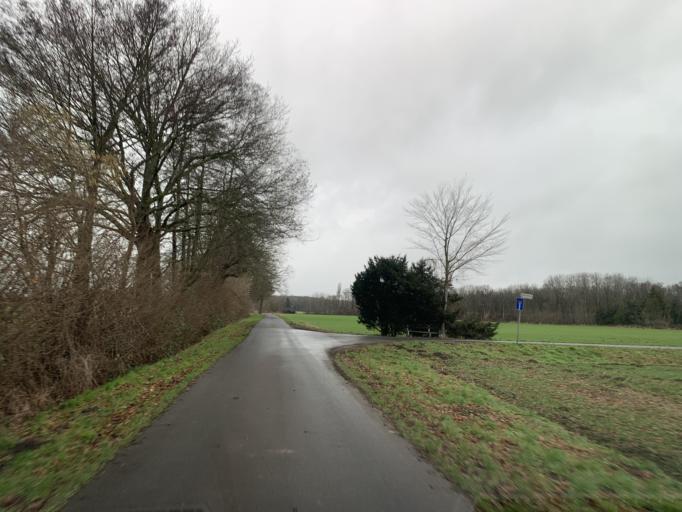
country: DE
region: North Rhine-Westphalia
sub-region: Regierungsbezirk Munster
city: Muenster
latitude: 51.9300
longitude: 7.5483
